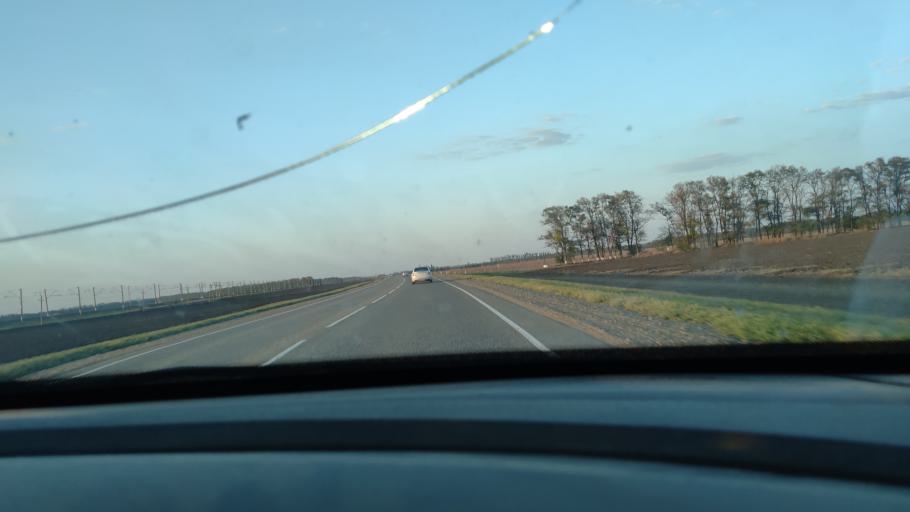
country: RU
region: Krasnodarskiy
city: Novominskaya
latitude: 46.3470
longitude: 38.9581
